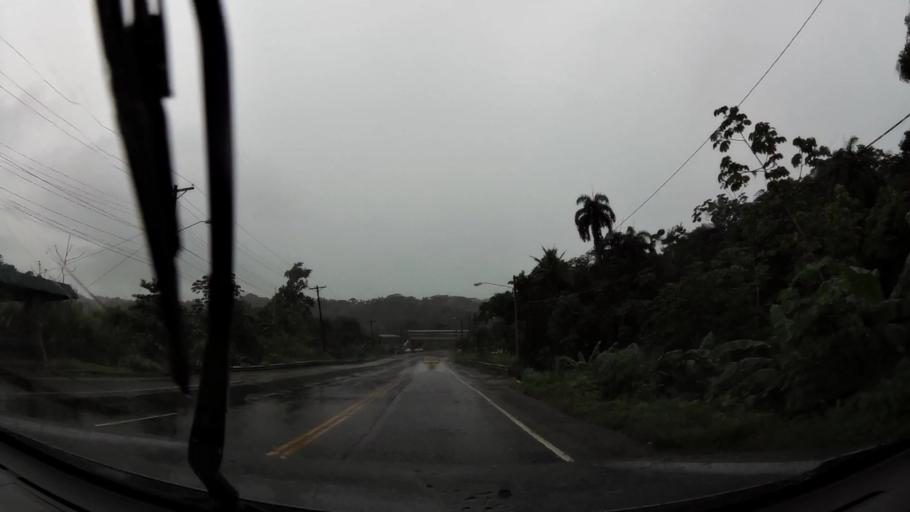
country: PA
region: Colon
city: Gatun
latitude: 9.2914
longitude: -79.7692
